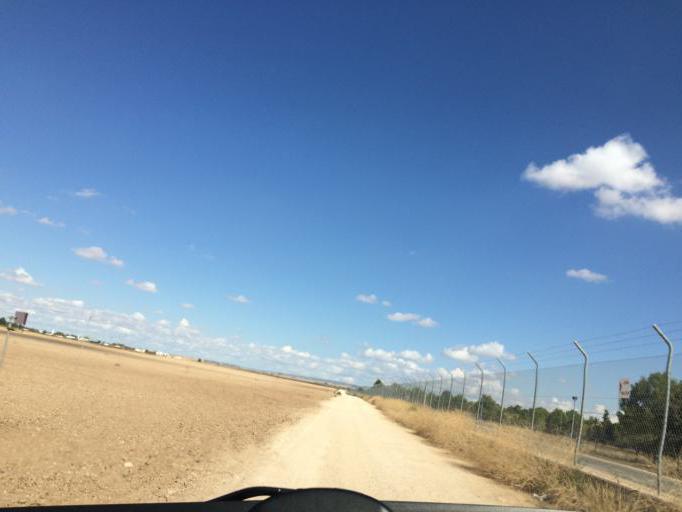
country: ES
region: Castille-La Mancha
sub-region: Provincia de Albacete
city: Albacete
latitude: 38.9578
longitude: -1.8582
